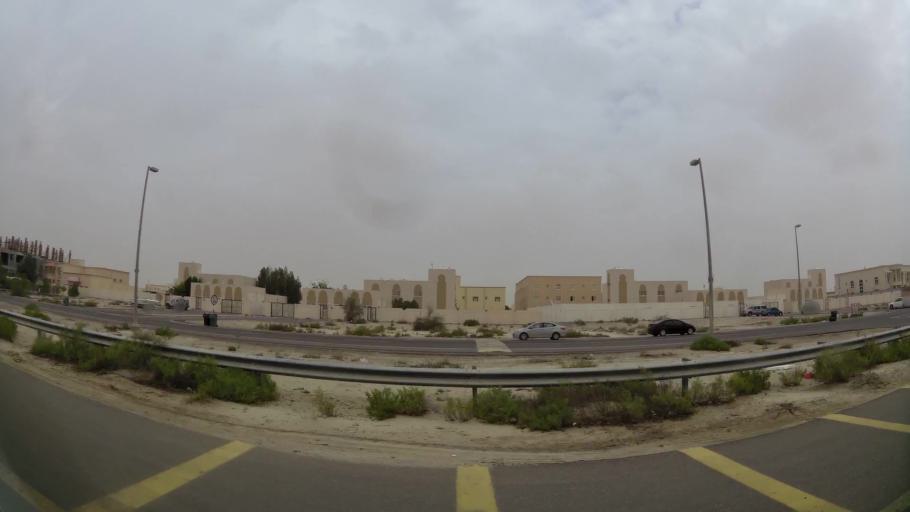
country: AE
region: Abu Dhabi
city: Abu Dhabi
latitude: 24.3908
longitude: 54.7133
